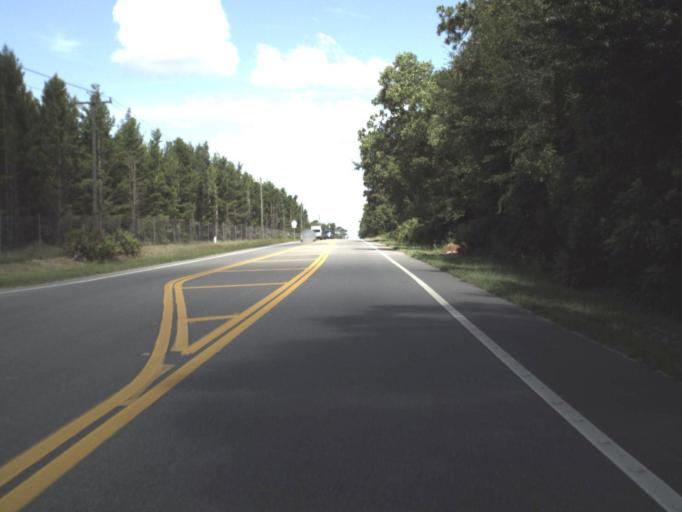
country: US
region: Florida
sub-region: Putnam County
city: Interlachen
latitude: 29.7282
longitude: -81.8505
